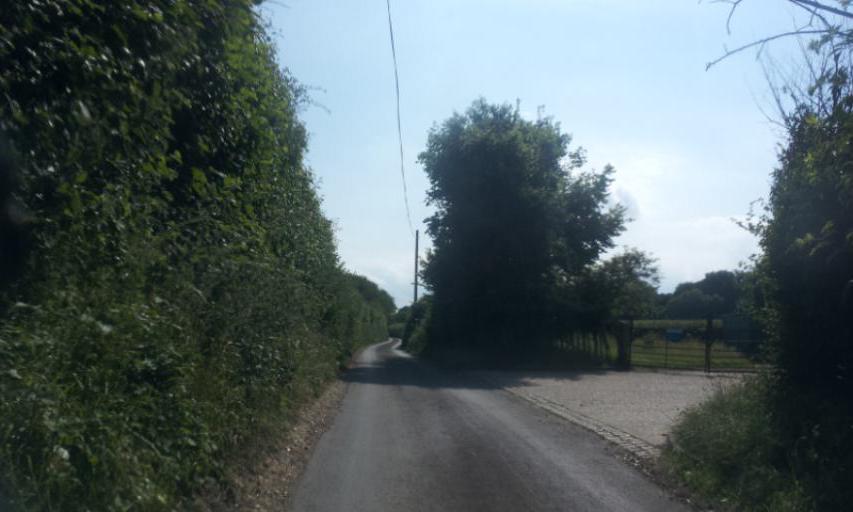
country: GB
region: England
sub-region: Kent
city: Teynham
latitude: 51.2801
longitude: 0.7693
